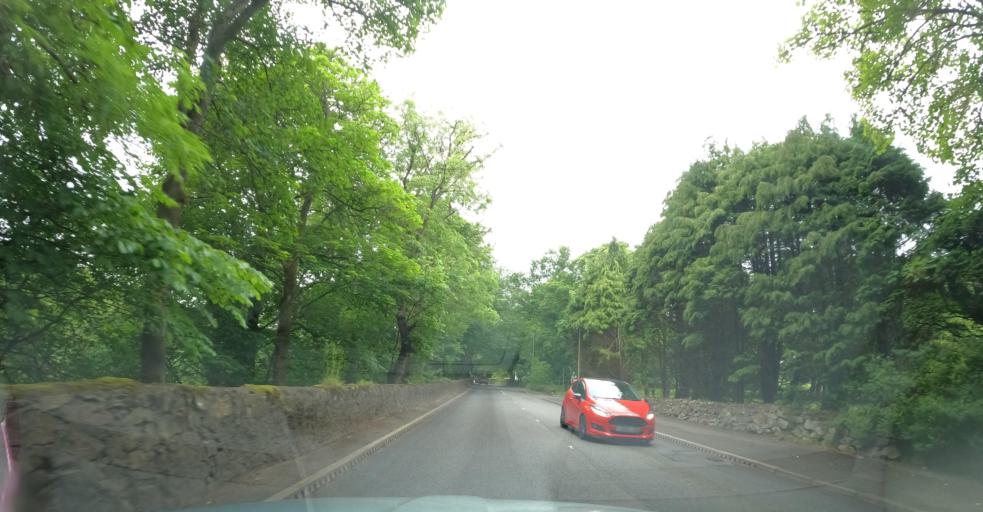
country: GB
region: Scotland
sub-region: Eilean Siar
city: Isle of Lewis
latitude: 58.2190
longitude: -6.3892
